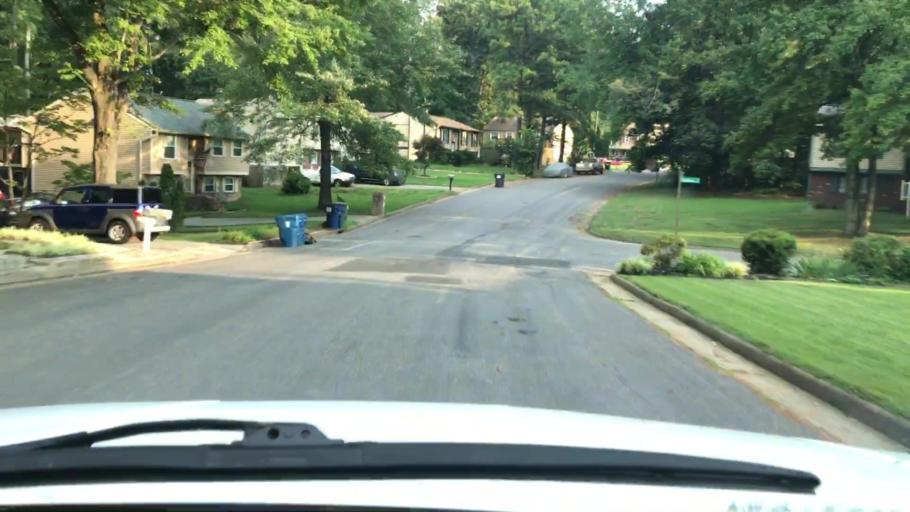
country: US
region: Virginia
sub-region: Chesterfield County
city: Chesterfield
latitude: 37.4408
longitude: -77.5157
